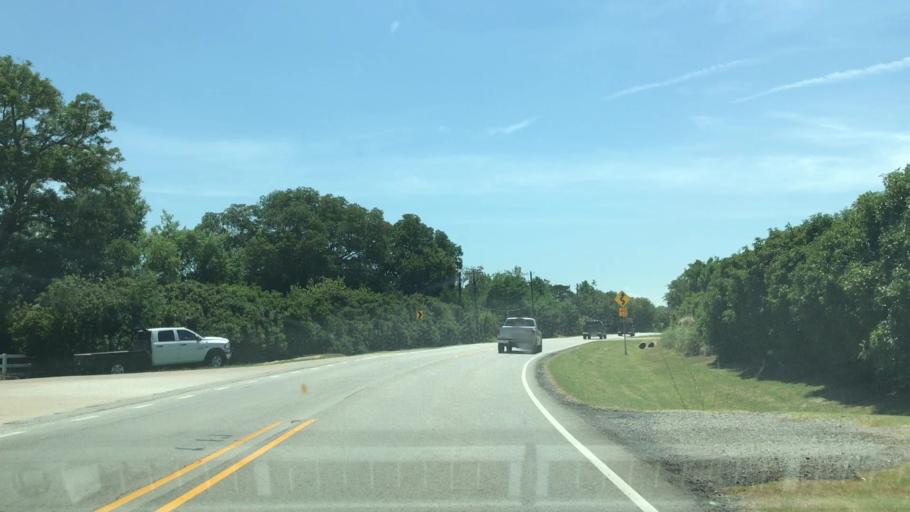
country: US
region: Texas
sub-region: Collin County
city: Lucas
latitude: 33.1091
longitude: -96.5984
